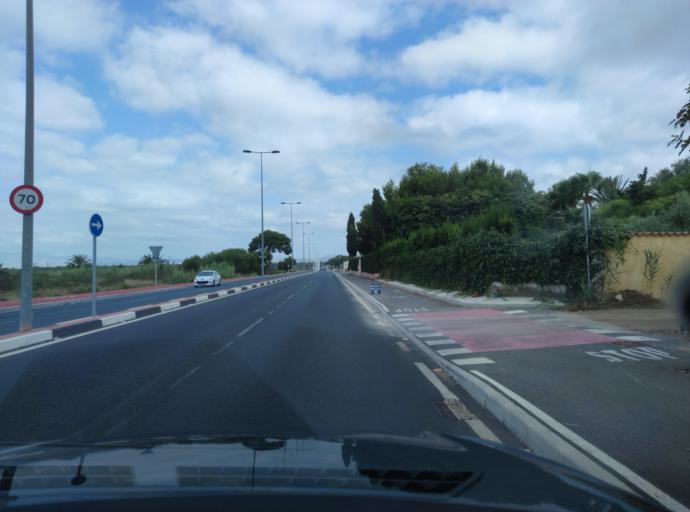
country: ES
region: Valencia
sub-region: Provincia de Alicante
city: Santa Pola
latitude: 38.2100
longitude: -0.5875
